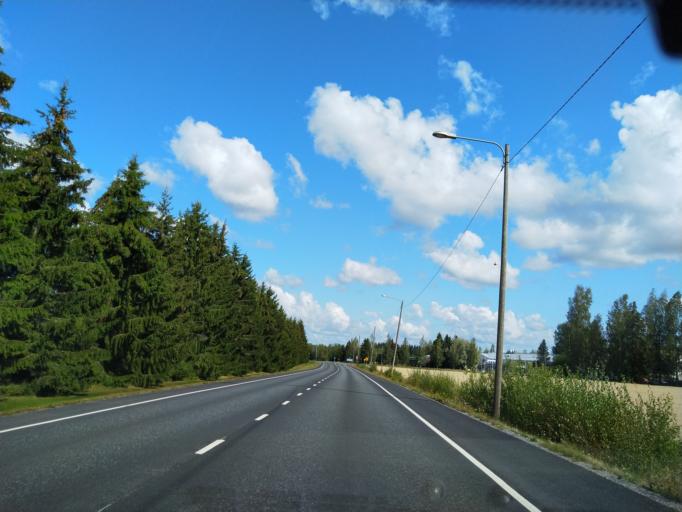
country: FI
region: Satakunta
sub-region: Pori
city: Huittinen
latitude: 61.1770
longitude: 22.7122
